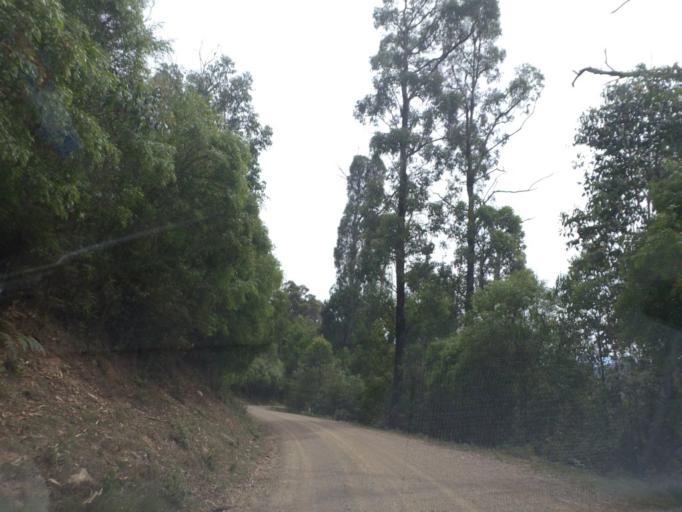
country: AU
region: Victoria
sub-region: Yarra Ranges
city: Healesville
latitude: -37.4558
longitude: 145.5721
